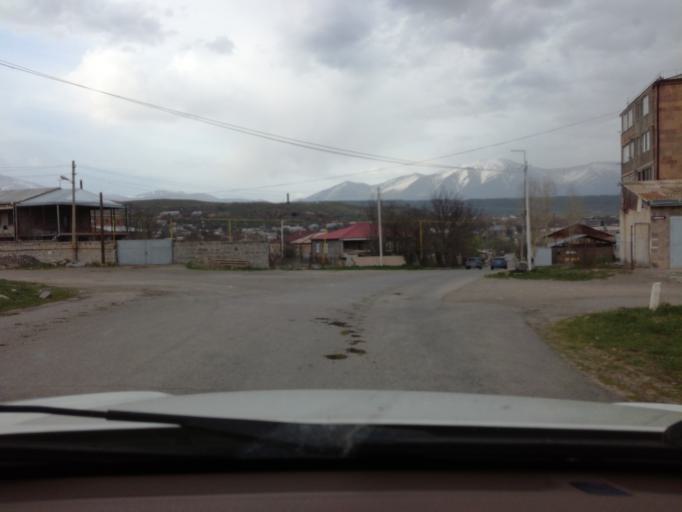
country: AM
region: Syunik'i Marz
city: Brrnakot'
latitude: 39.5219
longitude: 46.0140
